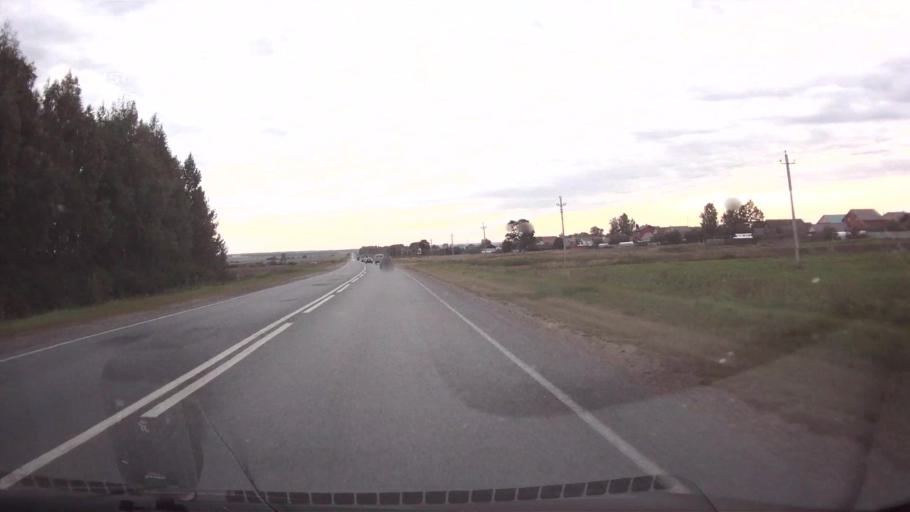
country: RU
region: Mariy-El
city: Yoshkar-Ola
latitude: 56.7146
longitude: 48.0946
